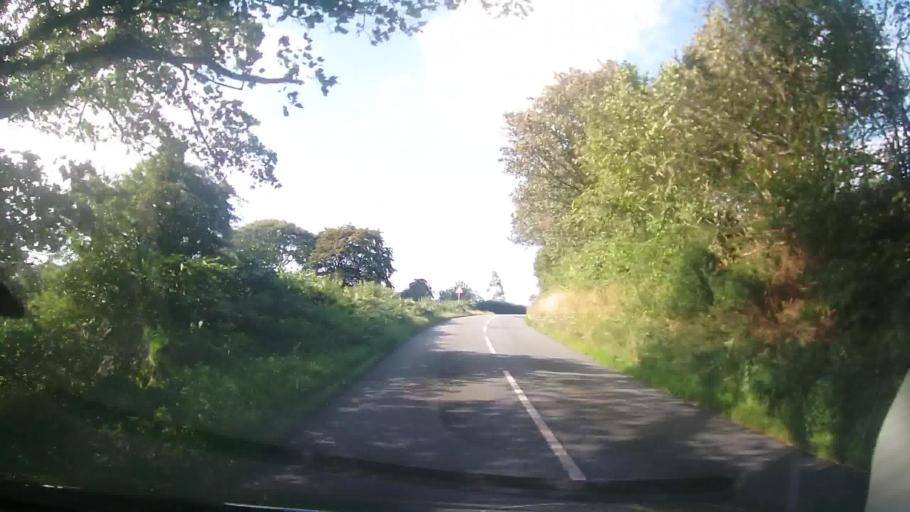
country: GB
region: England
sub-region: Shropshire
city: Pontesbury
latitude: 52.5909
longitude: -2.8804
